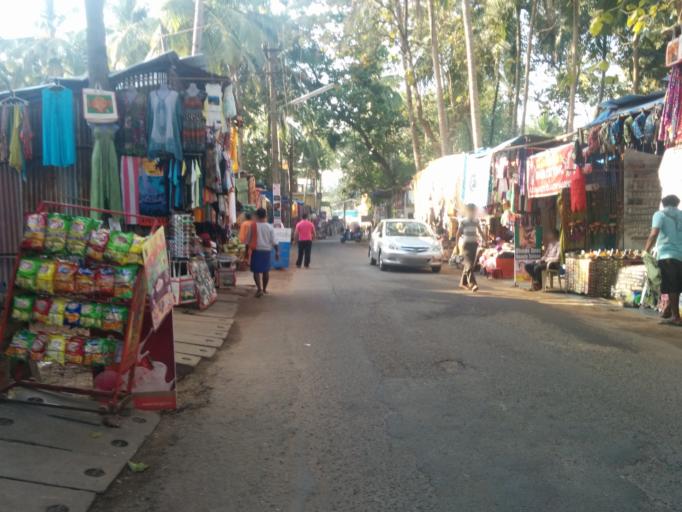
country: IN
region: Goa
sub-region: South Goa
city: Kankon
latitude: 15.0120
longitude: 74.0244
